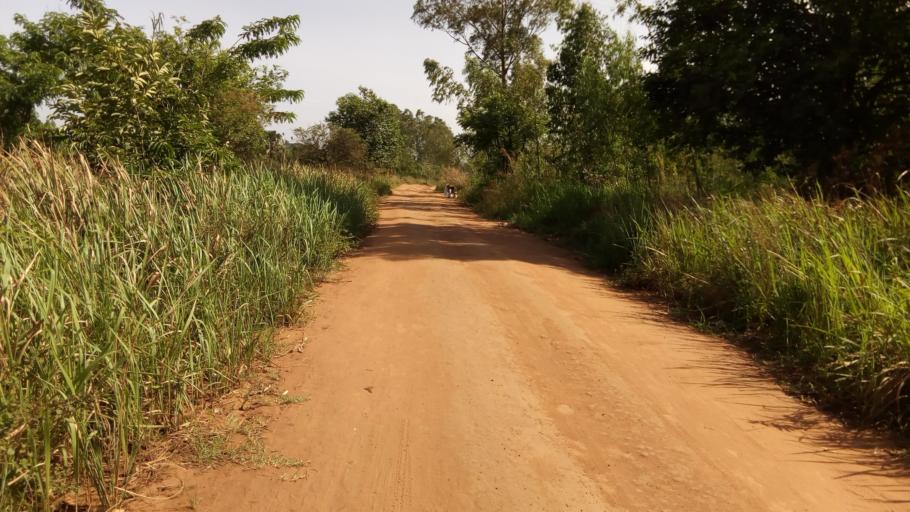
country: UG
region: Northern Region
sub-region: Gulu District
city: Gulu
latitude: 2.7985
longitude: 32.3281
